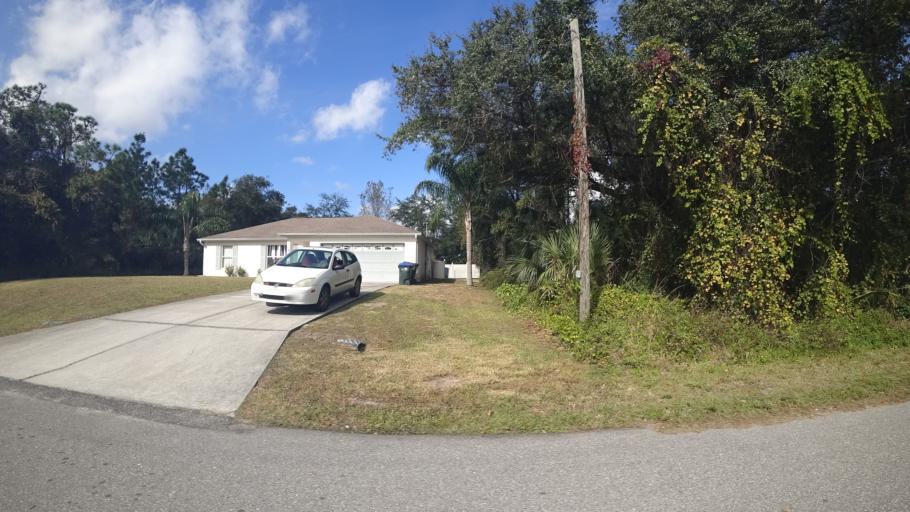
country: US
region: Florida
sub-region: Charlotte County
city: Port Charlotte
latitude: 27.0494
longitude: -82.1253
